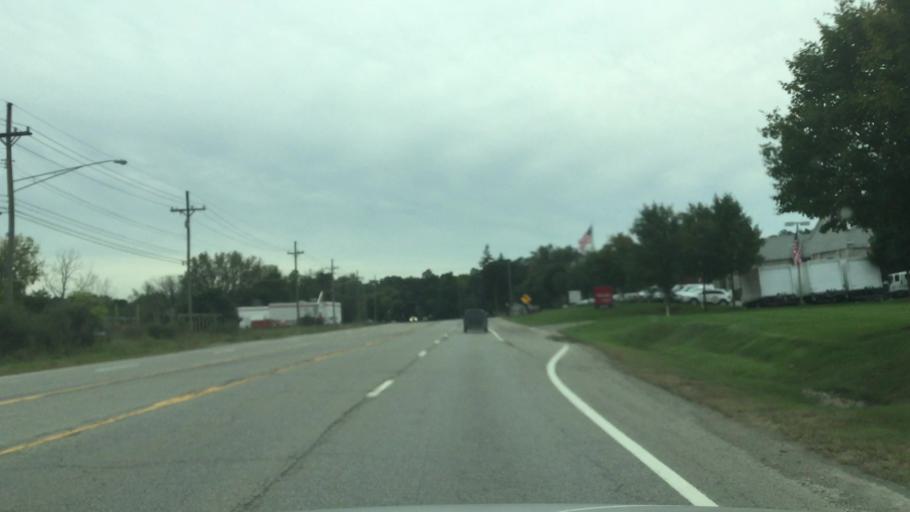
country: US
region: Michigan
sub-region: Oakland County
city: Clarkston
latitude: 42.7551
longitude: -83.4803
